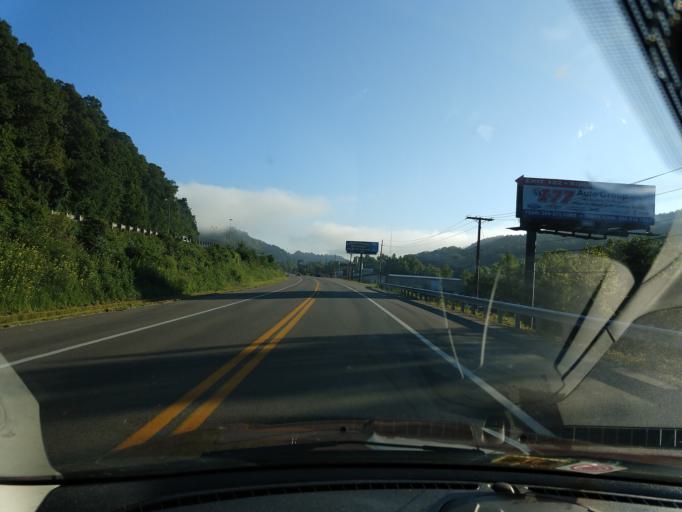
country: US
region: West Virginia
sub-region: Kanawha County
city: Charleston
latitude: 38.3718
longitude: -81.6065
